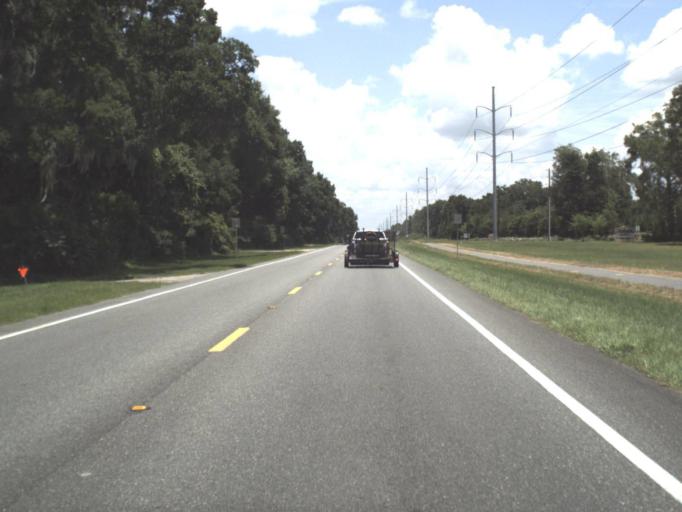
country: US
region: Florida
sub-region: Alachua County
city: Archer
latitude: 29.5861
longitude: -82.4457
